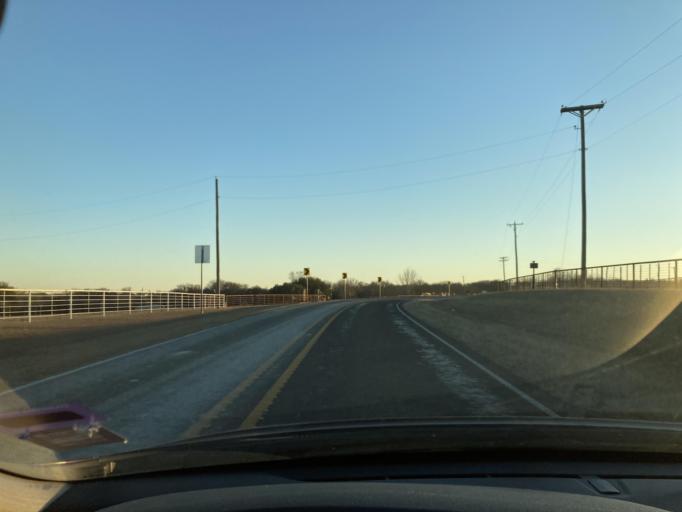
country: US
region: Texas
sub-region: Ellis County
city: Waxahachie
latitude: 32.3461
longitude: -96.8720
